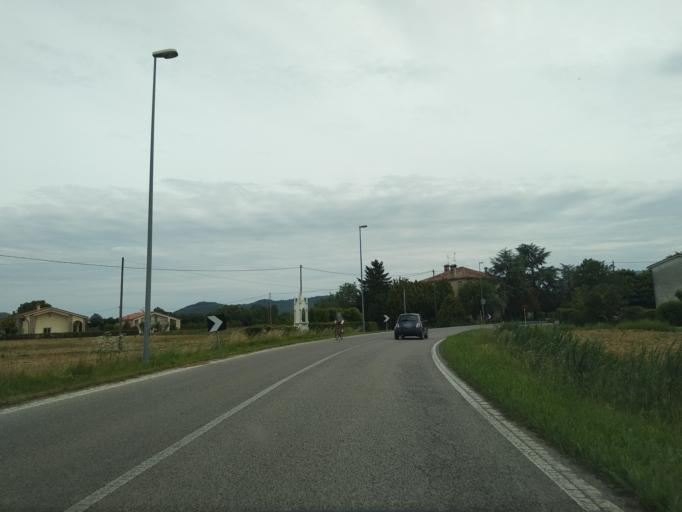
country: IT
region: Veneto
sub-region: Provincia di Padova
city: Montemerlo
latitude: 45.3945
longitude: 11.6986
